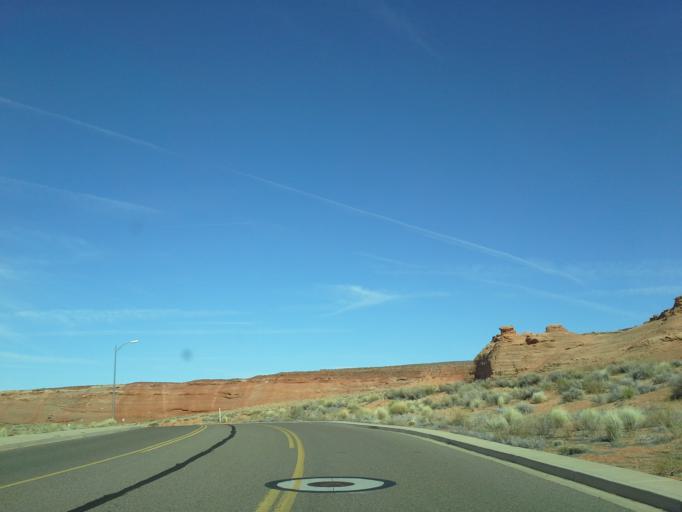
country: US
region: Arizona
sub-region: Coconino County
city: Page
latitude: 36.9317
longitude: -111.4695
